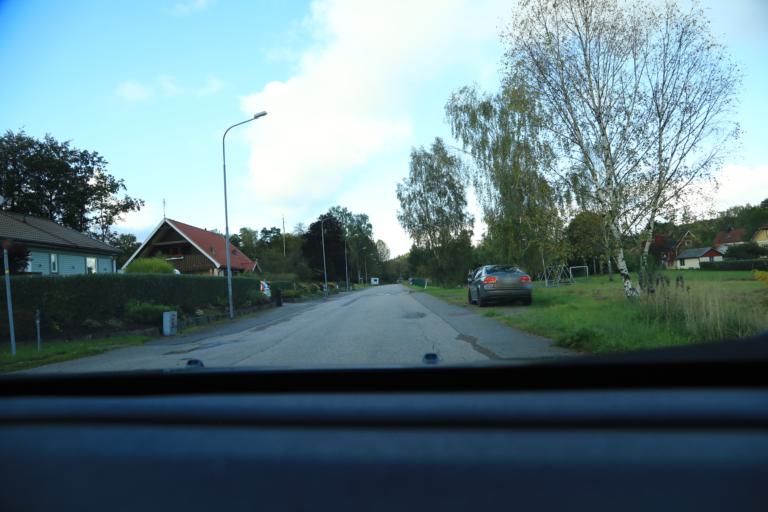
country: SE
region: Halland
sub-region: Halmstads Kommun
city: Getinge
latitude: 57.1422
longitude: 12.7226
